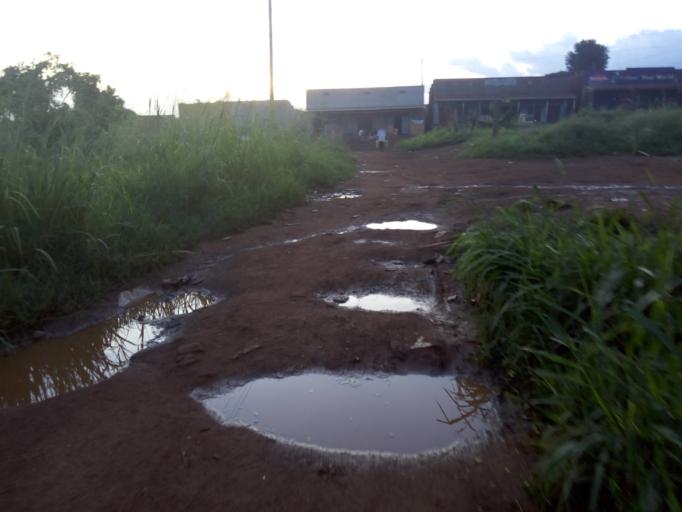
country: UG
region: Western Region
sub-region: Masindi District
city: Masindi
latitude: 1.6808
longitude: 31.7187
